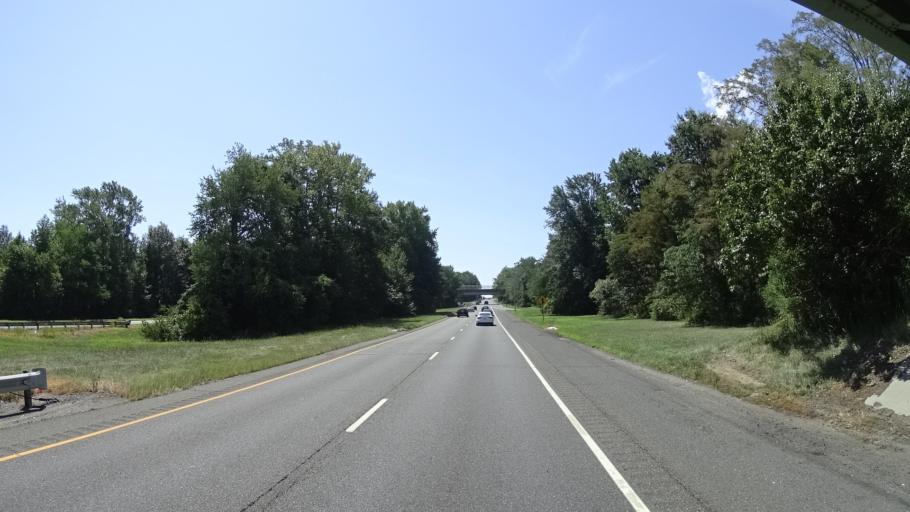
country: US
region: New Jersey
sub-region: Monmouth County
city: Wanamassa
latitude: 40.2528
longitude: -74.0564
